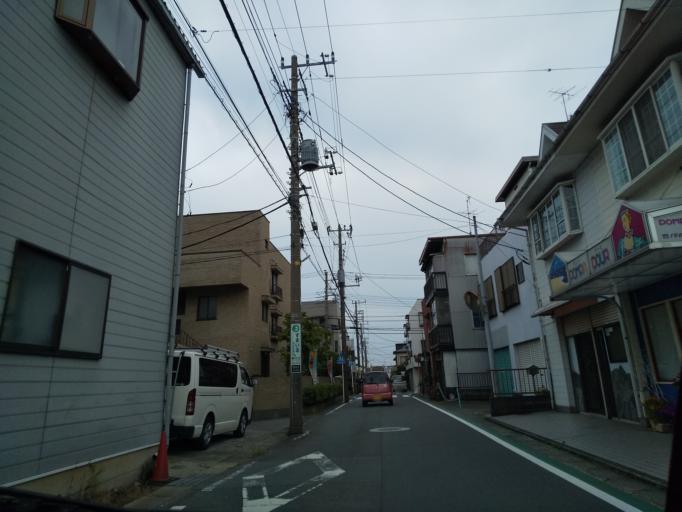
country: JP
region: Kanagawa
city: Atsugi
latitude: 35.4686
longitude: 139.3555
